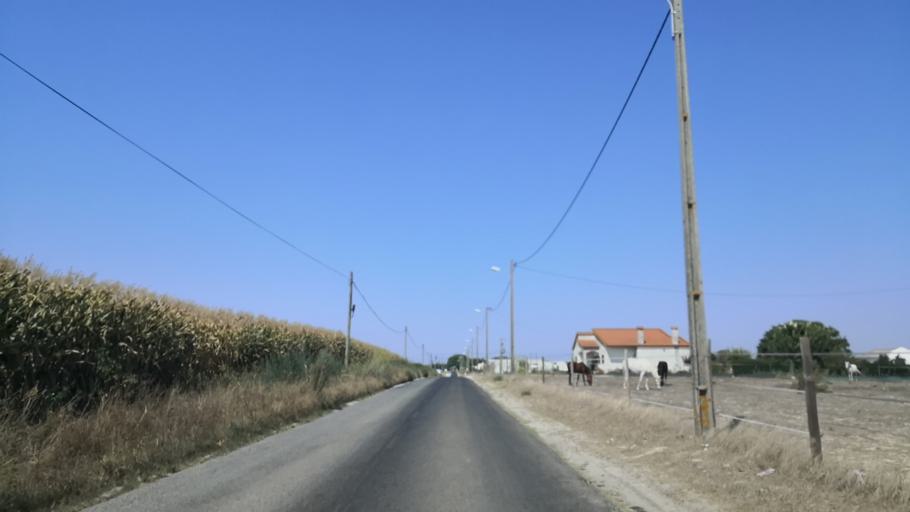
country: PT
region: Santarem
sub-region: Benavente
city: Poceirao
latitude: 38.7078
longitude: -8.7186
